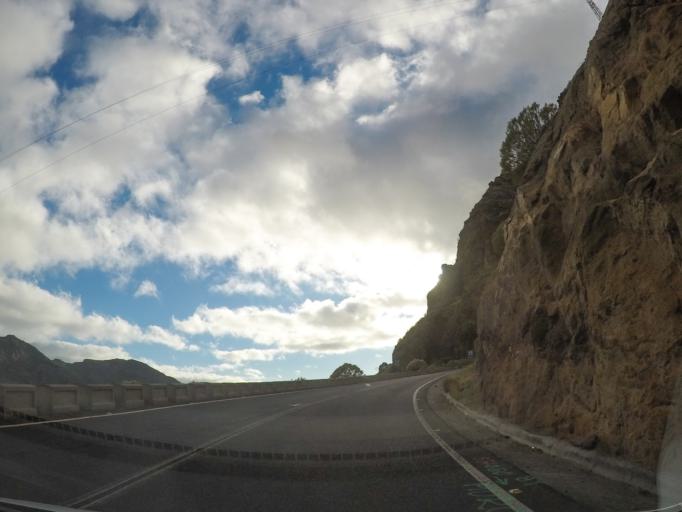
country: ES
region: Canary Islands
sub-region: Provincia de Santa Cruz de Tenerife
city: Vallehermosa
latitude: 28.1186
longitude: -17.3136
